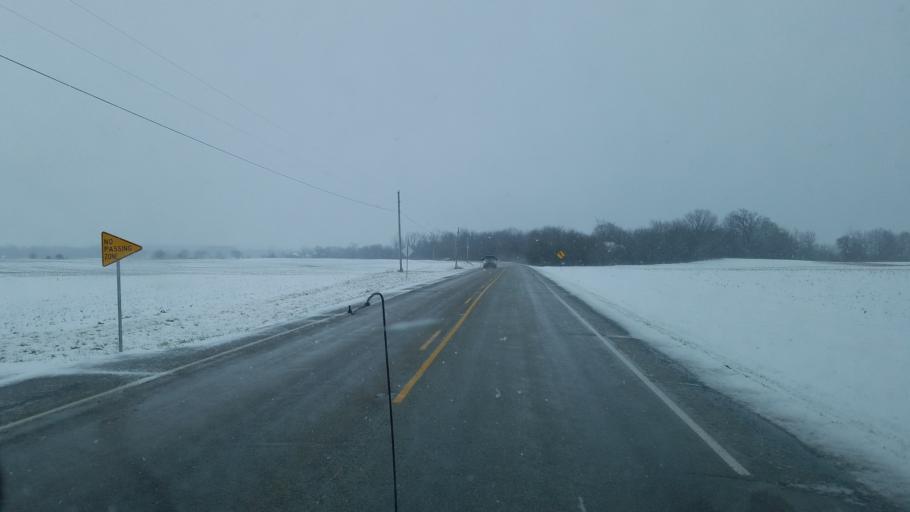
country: US
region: Indiana
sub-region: Randolph County
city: Lynn
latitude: 39.9614
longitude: -85.0215
